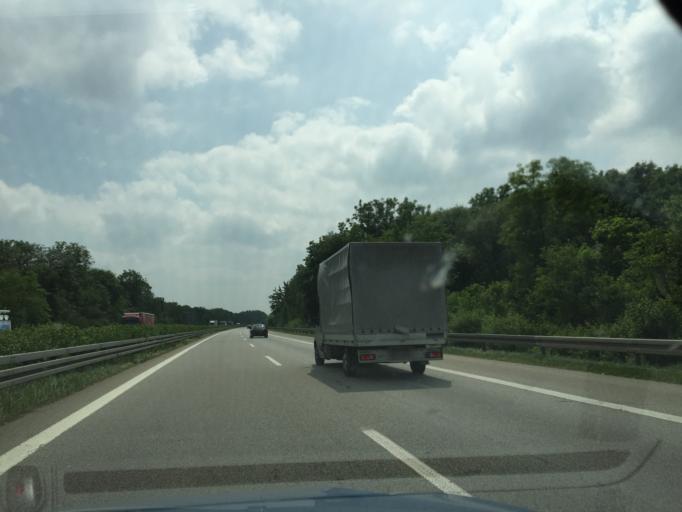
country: DE
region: Bavaria
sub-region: Swabia
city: Nersingen
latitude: 48.4486
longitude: 10.1158
